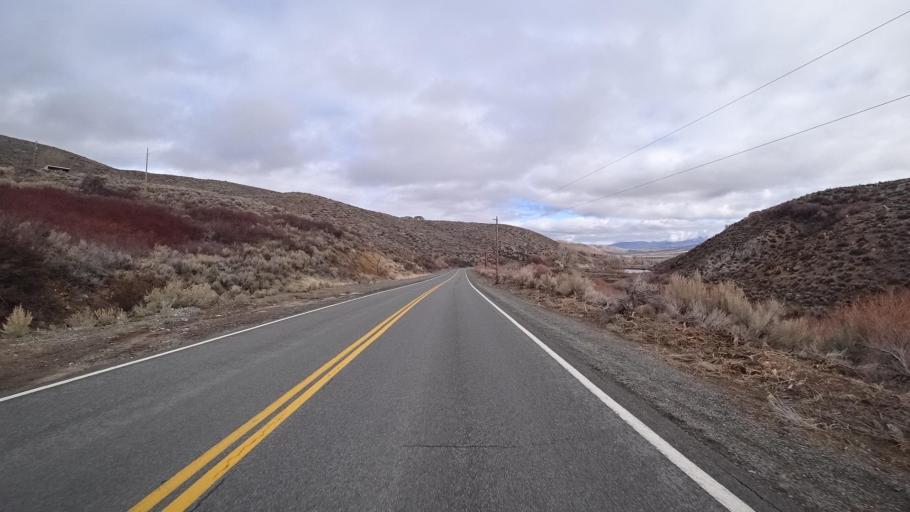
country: US
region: Nevada
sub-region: Washoe County
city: Cold Springs
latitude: 39.8277
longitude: -119.9381
